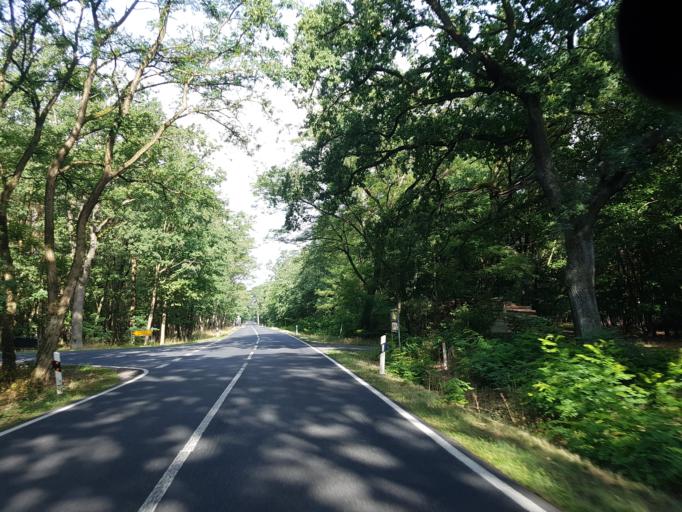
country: DE
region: Brandenburg
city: Ihlow
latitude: 51.9921
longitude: 13.2646
